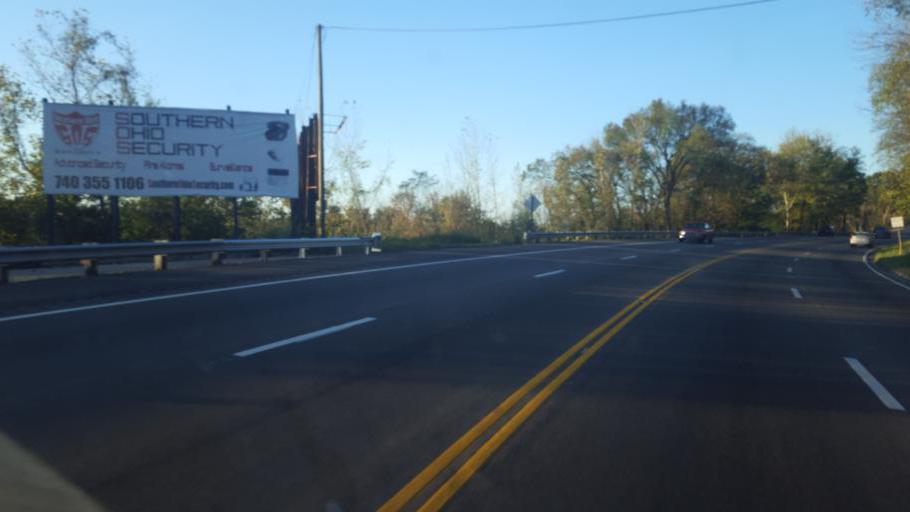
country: US
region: Ohio
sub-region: Scioto County
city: Rosemount
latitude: 38.7623
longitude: -82.9904
